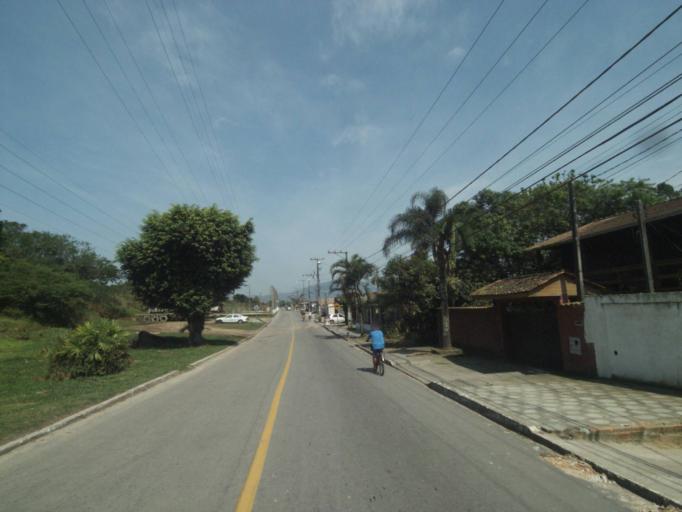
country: BR
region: Parana
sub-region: Paranagua
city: Paranagua
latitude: -25.5413
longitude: -48.5453
